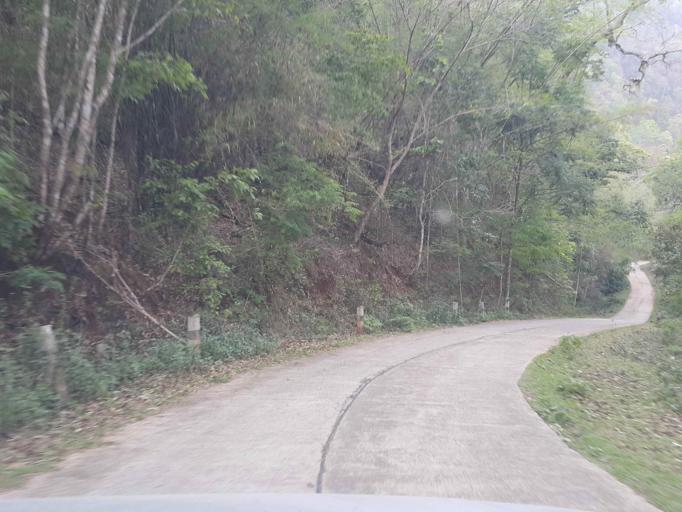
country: TH
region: Chiang Mai
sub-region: Amphoe Chiang Dao
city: Chiang Dao
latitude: 19.3879
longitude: 98.7695
